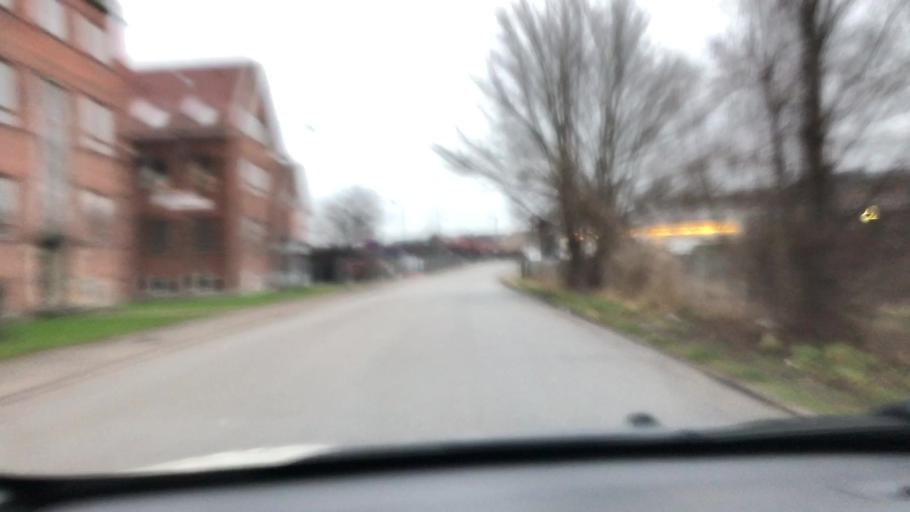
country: DK
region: Capital Region
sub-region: Glostrup Kommune
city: Glostrup
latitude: 55.6603
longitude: 12.3947
